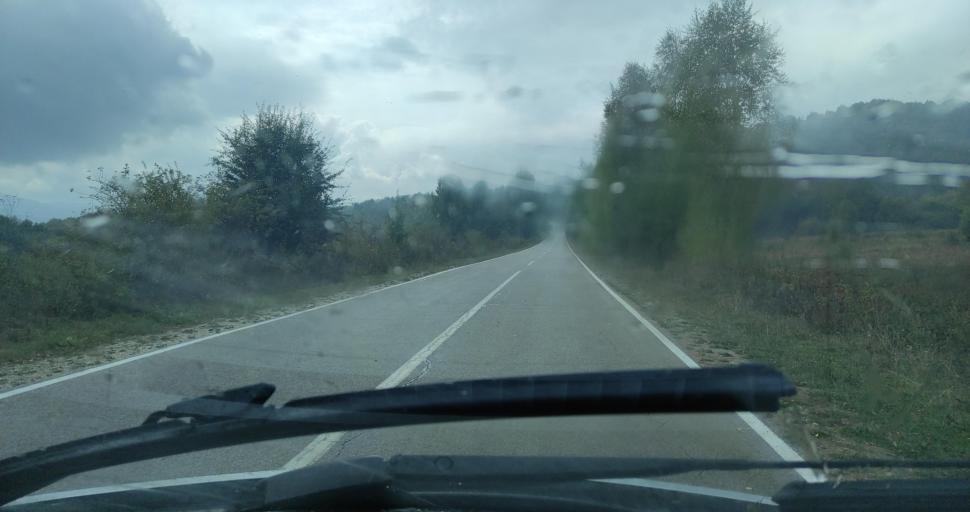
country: RS
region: Central Serbia
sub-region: Jablanicki Okrug
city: Crna Trava
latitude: 42.7202
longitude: 22.3341
